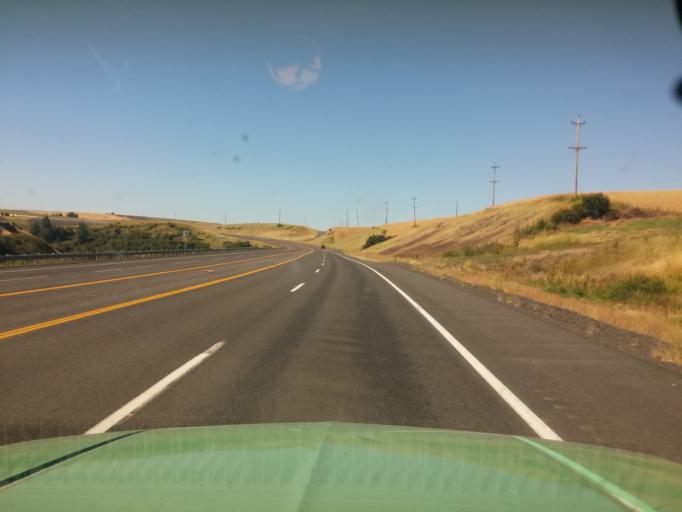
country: US
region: Washington
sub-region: Asotin County
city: Clarkston
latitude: 46.4853
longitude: -117.0342
